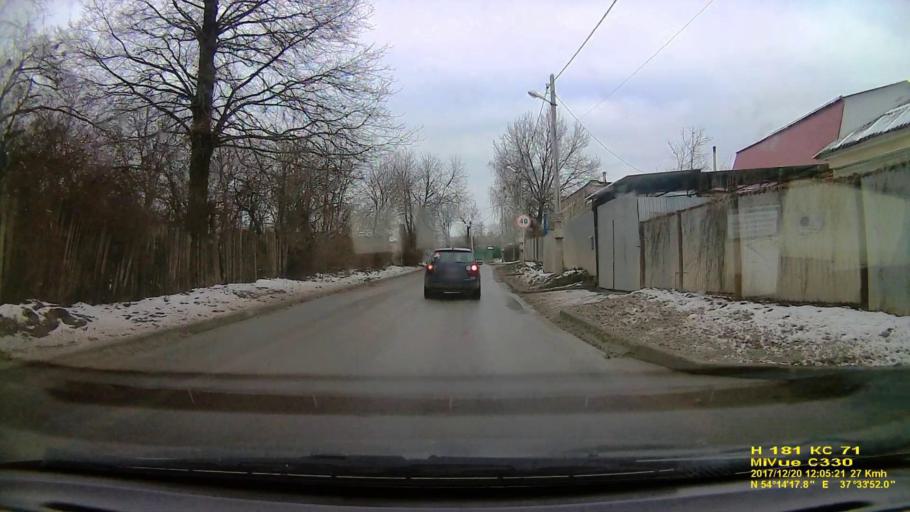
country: RU
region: Tula
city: Gorelki
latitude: 54.2385
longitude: 37.5644
